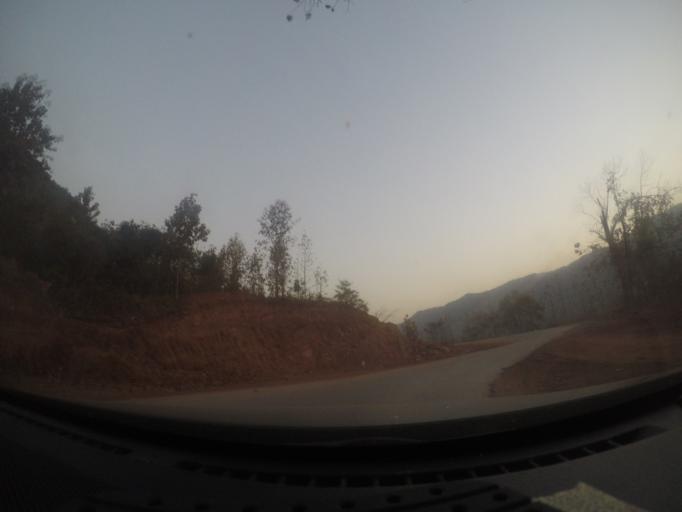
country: MM
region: Mandalay
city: Yamethin
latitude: 20.7202
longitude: 96.4993
